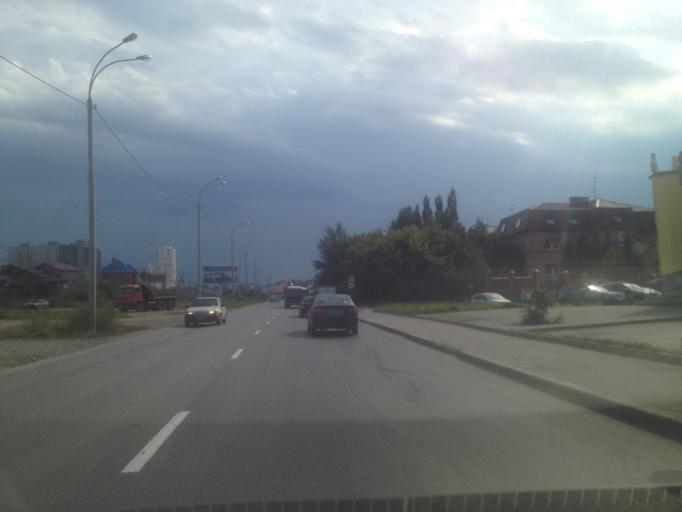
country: RU
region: Sverdlovsk
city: Shirokaya Rechka
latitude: 56.8077
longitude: 60.4969
